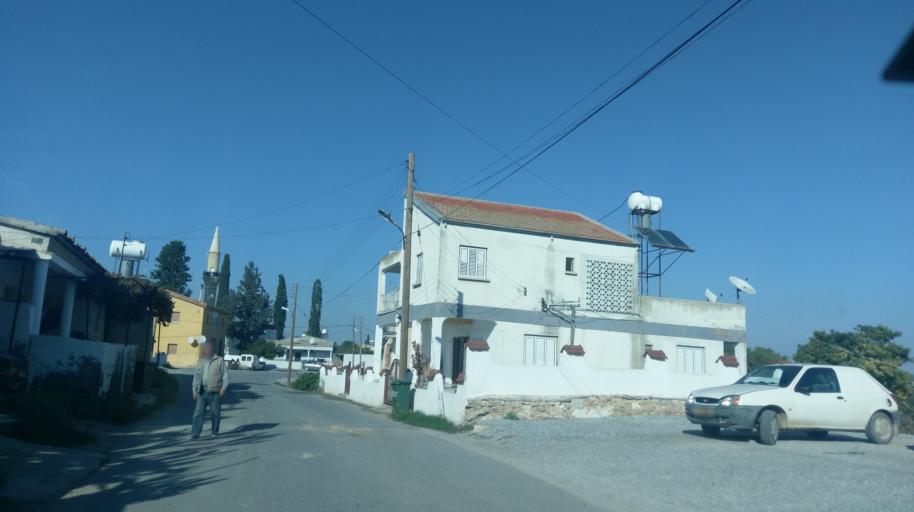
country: CY
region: Larnaka
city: Troulloi
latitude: 35.0885
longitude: 33.6284
